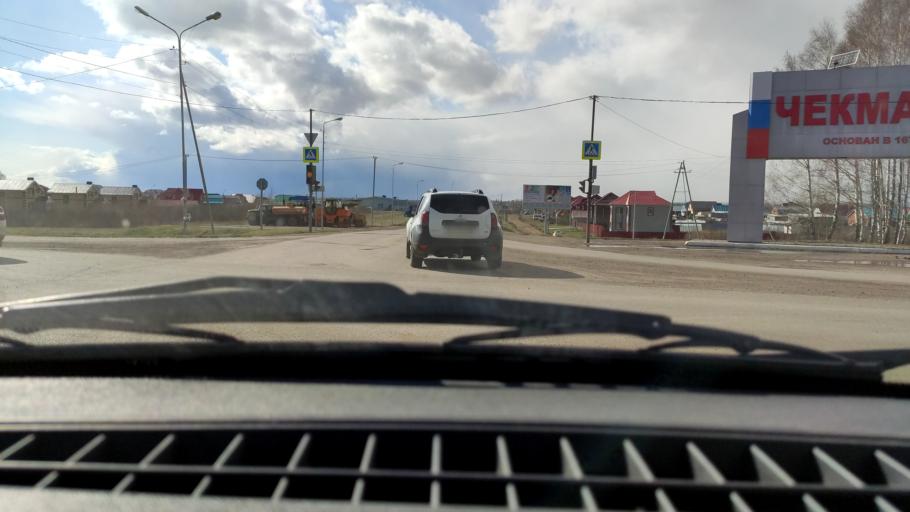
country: RU
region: Bashkortostan
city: Chekmagush
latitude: 55.1300
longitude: 54.6846
